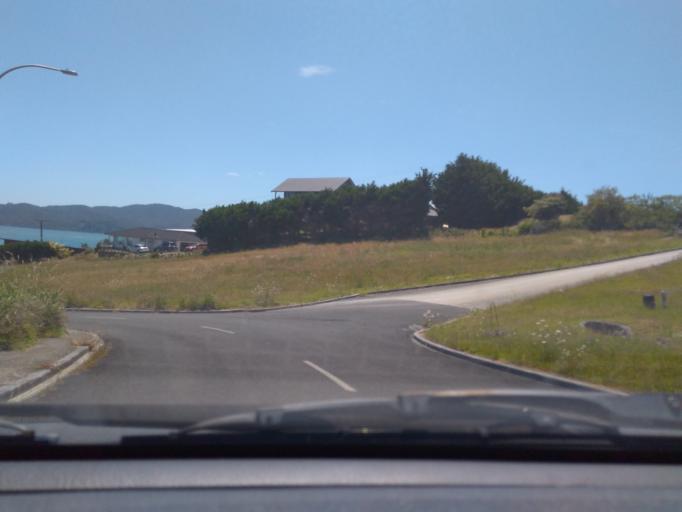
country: NZ
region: Northland
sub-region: Far North District
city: Taipa
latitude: -34.9955
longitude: 173.5089
